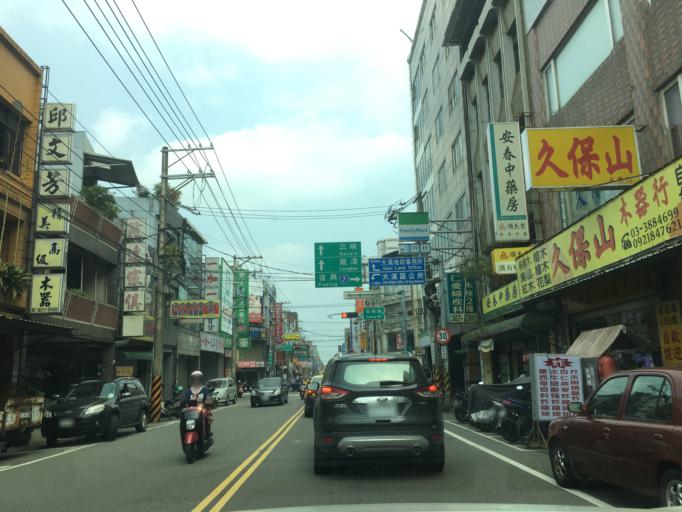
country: TW
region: Taiwan
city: Daxi
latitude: 24.8802
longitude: 121.2886
